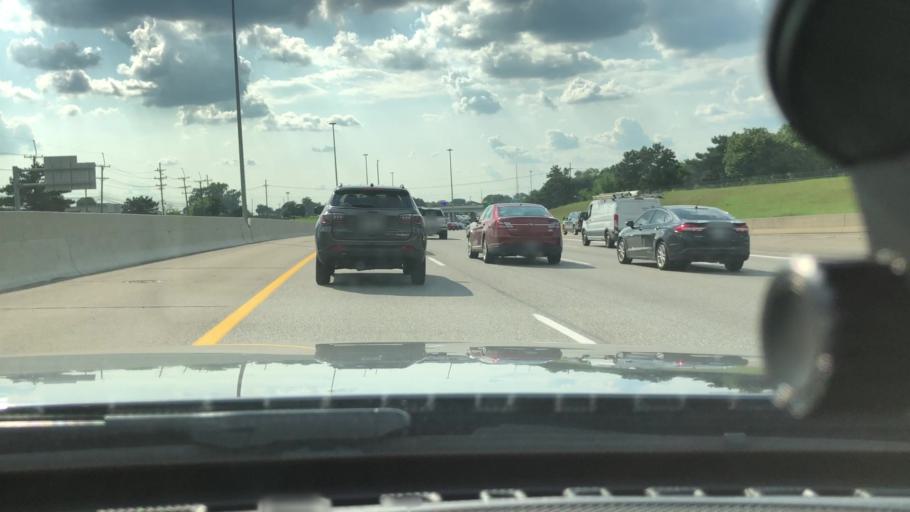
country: US
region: Michigan
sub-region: Wayne County
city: Plymouth
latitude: 42.3809
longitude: -83.4192
